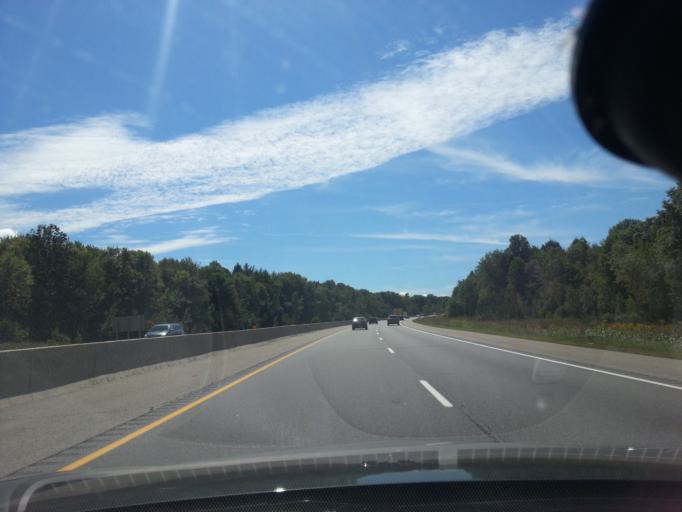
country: CA
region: Ontario
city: Brockville
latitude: 44.5701
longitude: -75.7387
